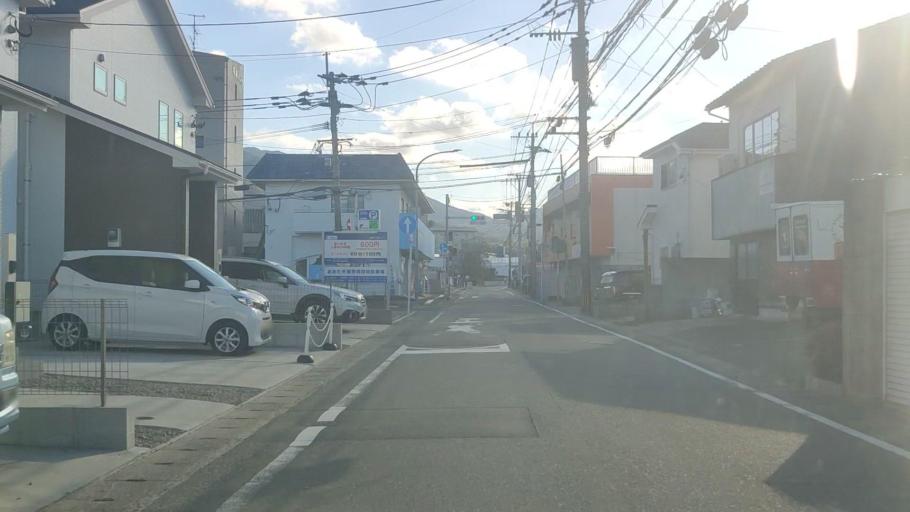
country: JP
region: Fukuoka
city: Fukuoka-shi
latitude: 33.5498
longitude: 130.3575
